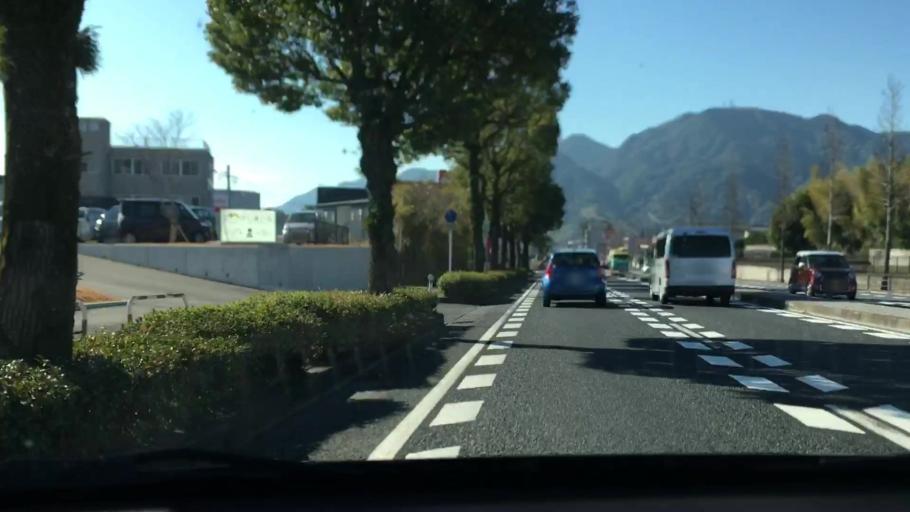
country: JP
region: Kagoshima
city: Kajiki
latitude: 31.7203
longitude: 130.6212
